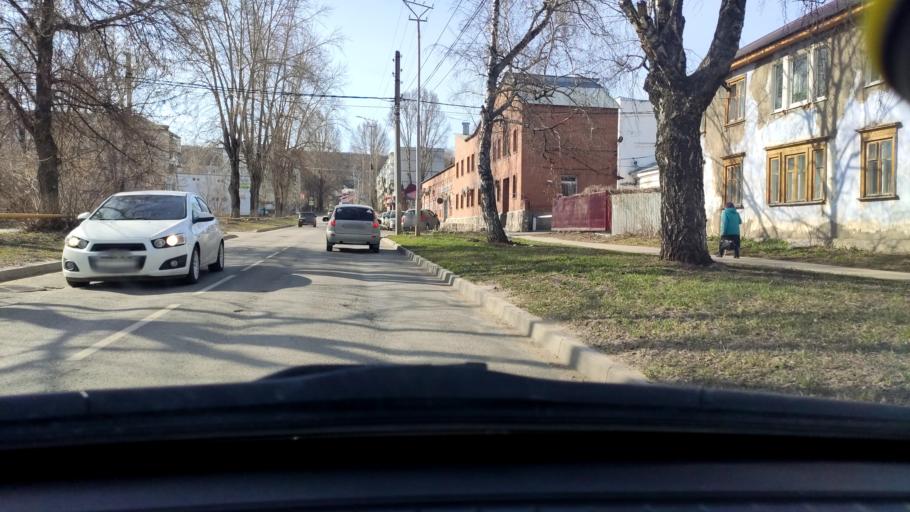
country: RU
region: Samara
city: Zhigulevsk
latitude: 53.3975
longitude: 49.4975
